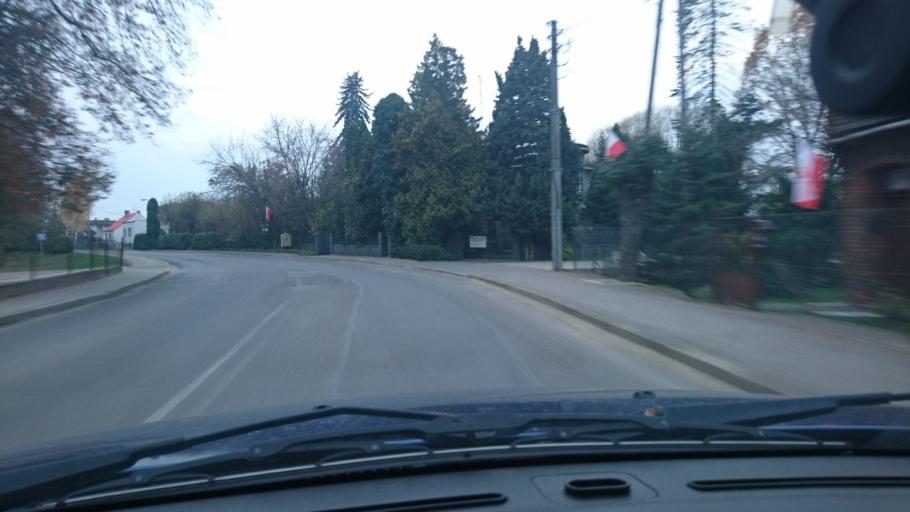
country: PL
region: Greater Poland Voivodeship
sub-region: Powiat ostrowski
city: Odolanow
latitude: 51.5736
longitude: 17.6690
